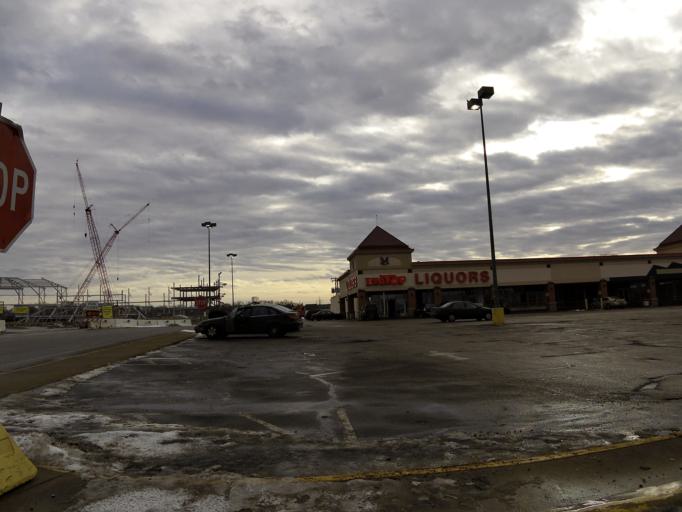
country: US
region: Minnesota
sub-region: Ramsey County
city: Falcon Heights
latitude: 44.9548
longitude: -93.1661
